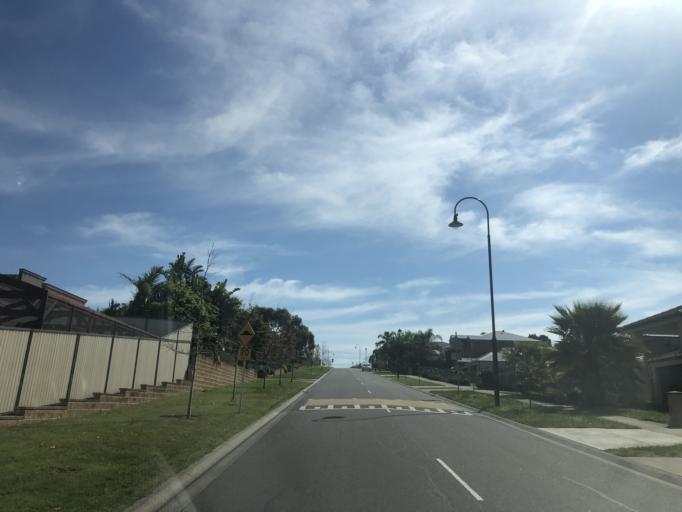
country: AU
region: Victoria
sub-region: Casey
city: Narre Warren North
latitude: -37.9928
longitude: 145.2917
